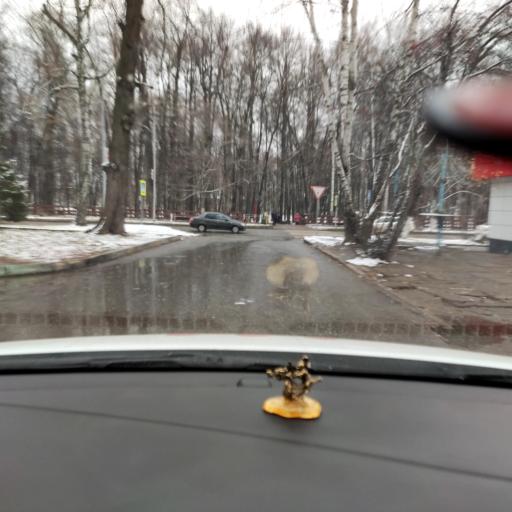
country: RU
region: Tatarstan
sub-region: Zelenodol'skiy Rayon
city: Zelenodolsk
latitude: 55.8458
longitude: 48.5074
